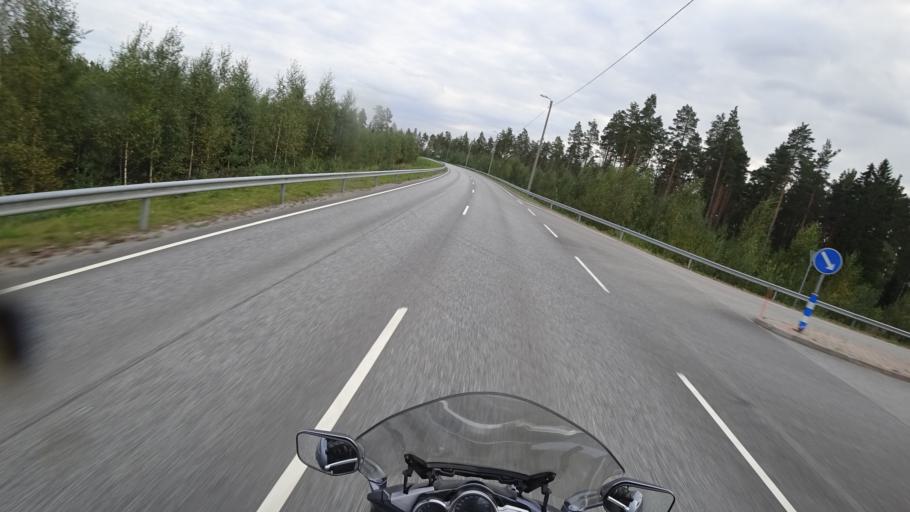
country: FI
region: Uusimaa
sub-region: Raaseporin
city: Karis
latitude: 60.0650
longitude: 23.6300
